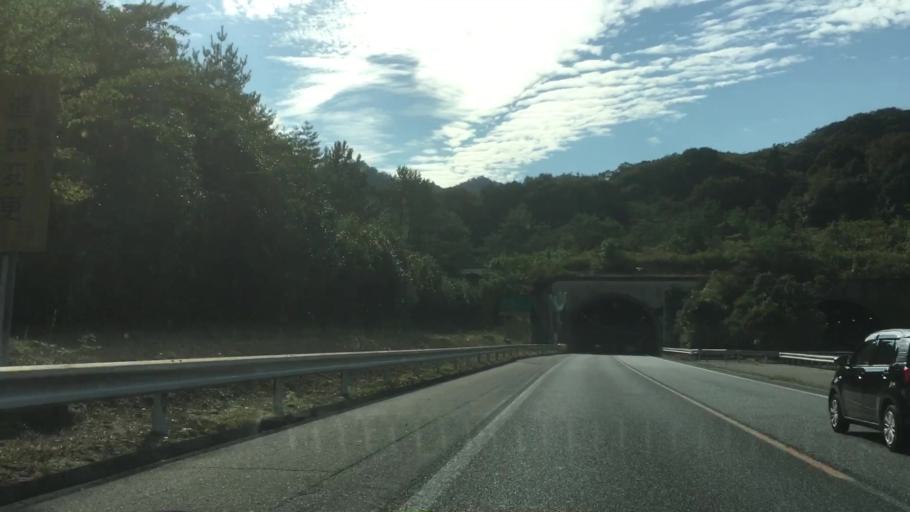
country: JP
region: Yamaguchi
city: Yanai
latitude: 34.0624
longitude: 132.0423
